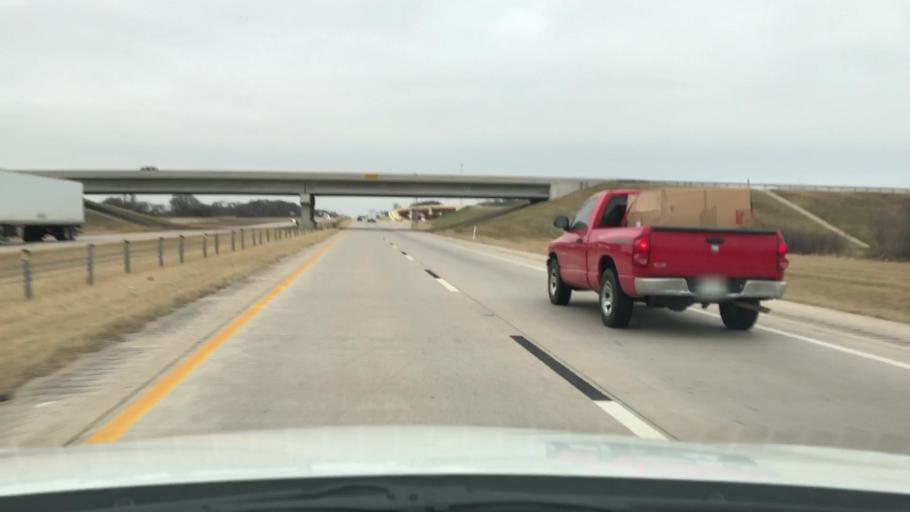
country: US
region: Texas
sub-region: Cooke County
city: Gainesville
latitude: 33.7649
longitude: -97.1348
